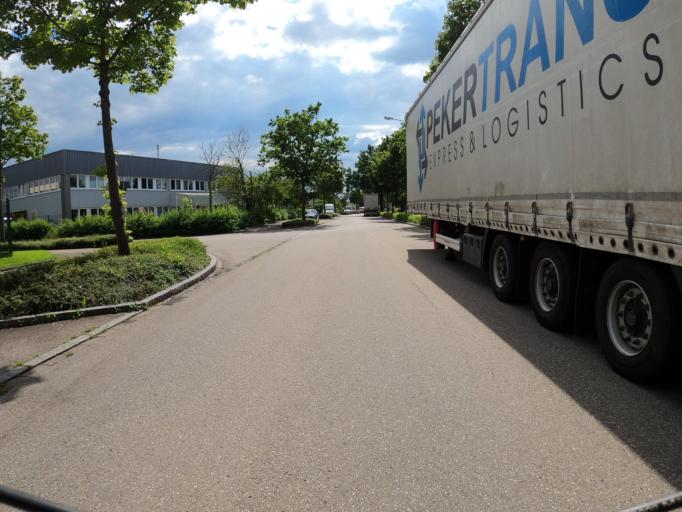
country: DE
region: Bavaria
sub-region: Swabia
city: Neu-Ulm
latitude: 48.3912
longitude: 10.0444
